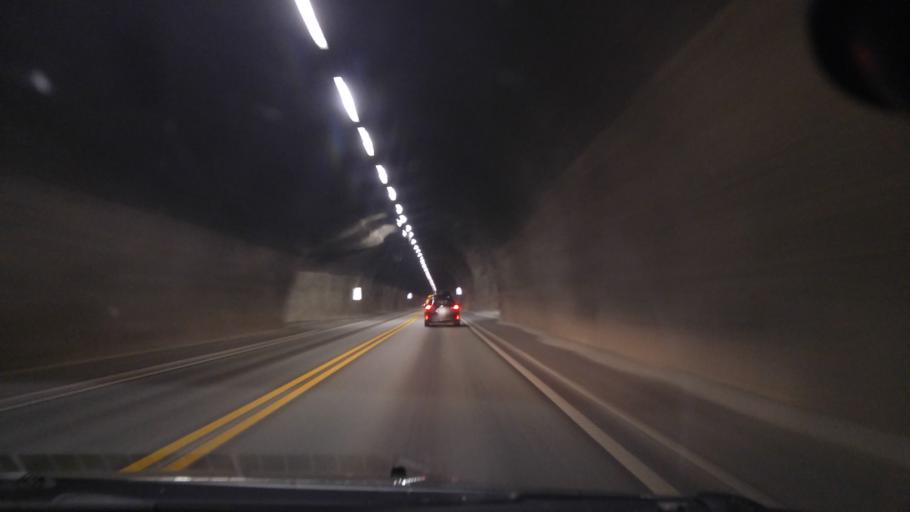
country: NO
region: Sor-Trondelag
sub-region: Malvik
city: Malvik
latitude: 63.4222
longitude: 10.6036
